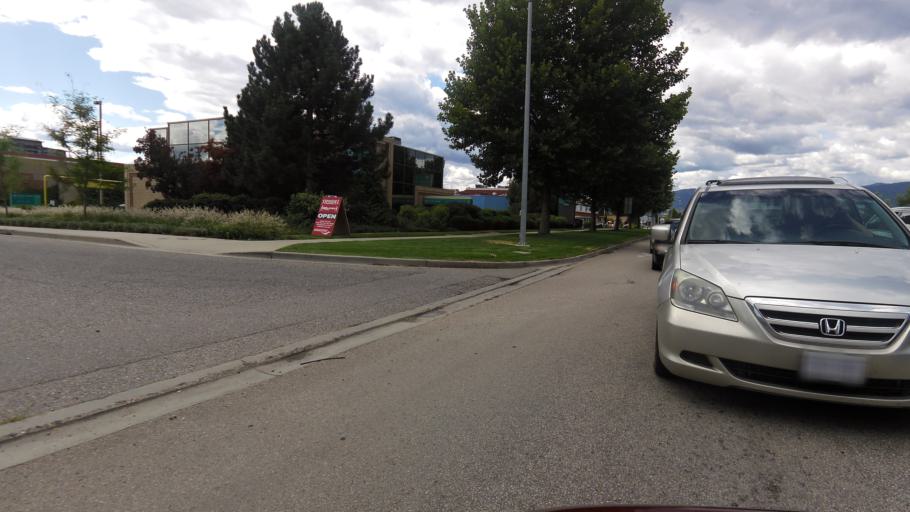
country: CA
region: British Columbia
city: Kelowna
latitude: 49.8818
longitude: -119.4451
